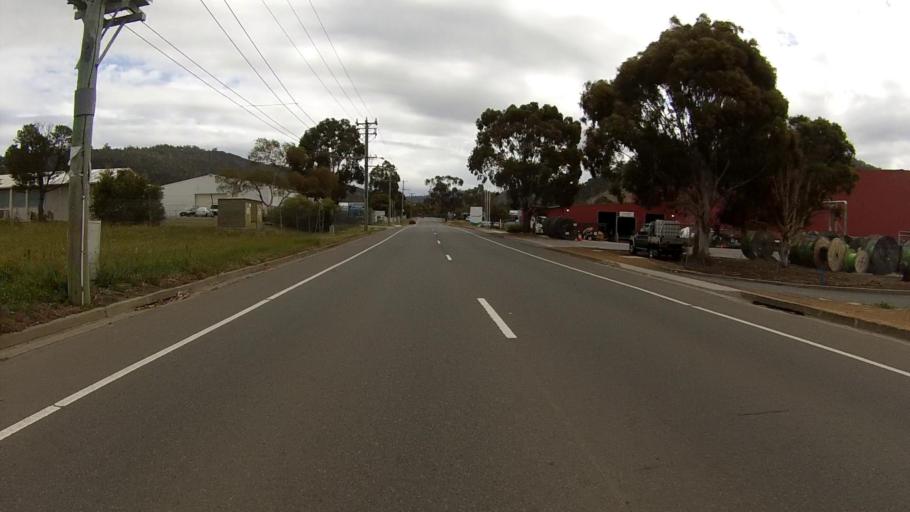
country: AU
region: Tasmania
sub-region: Clarence
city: Cambridge
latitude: -42.8344
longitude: 147.4517
